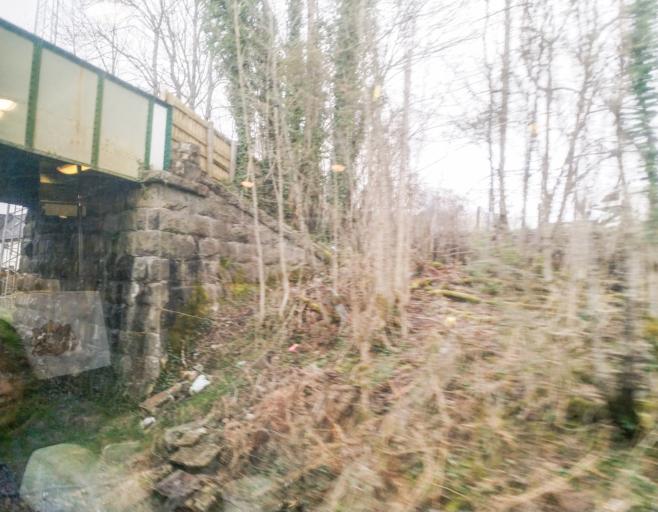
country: GB
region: Scotland
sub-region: Highland
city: Spean Bridge
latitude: 56.8884
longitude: -4.8366
